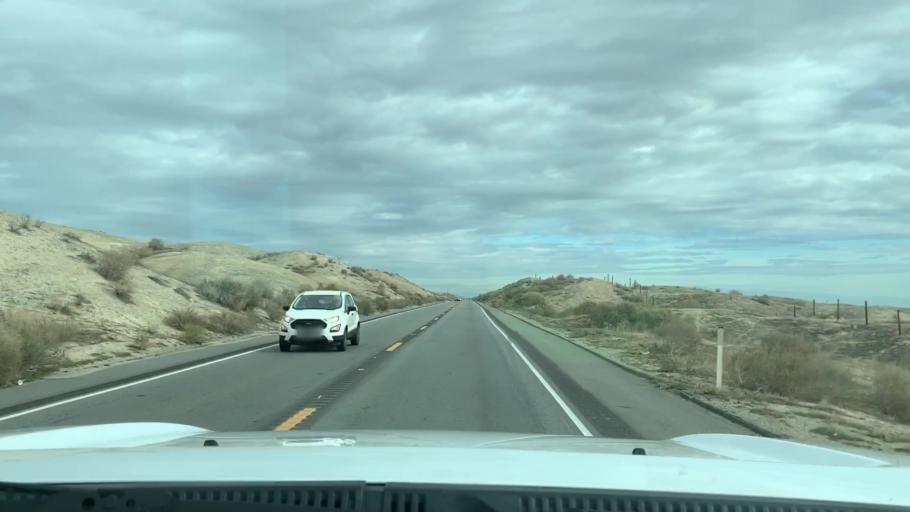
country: US
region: California
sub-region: Kern County
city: Ford City
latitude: 35.2355
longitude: -119.3656
